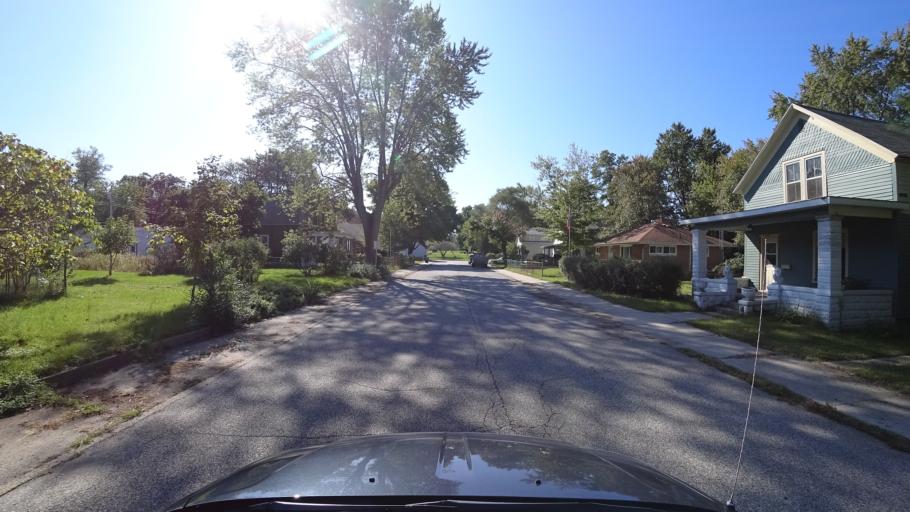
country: US
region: Indiana
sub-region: LaPorte County
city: Michigan City
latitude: 41.7068
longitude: -86.8820
